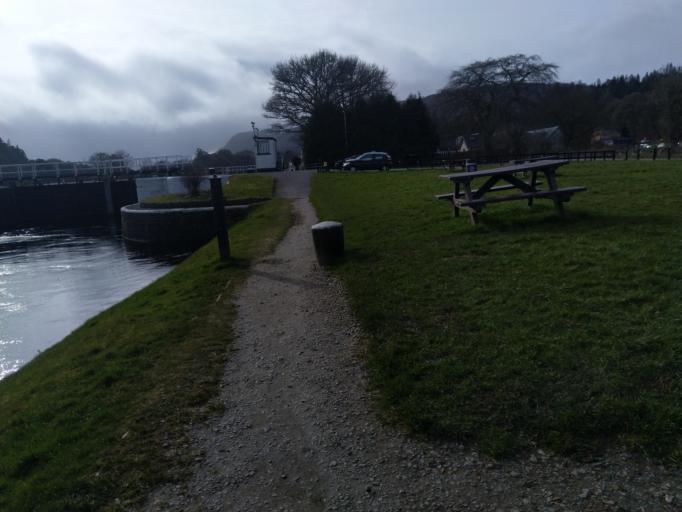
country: GB
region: Scotland
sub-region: Highland
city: Inverness
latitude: 57.4336
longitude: -4.3016
